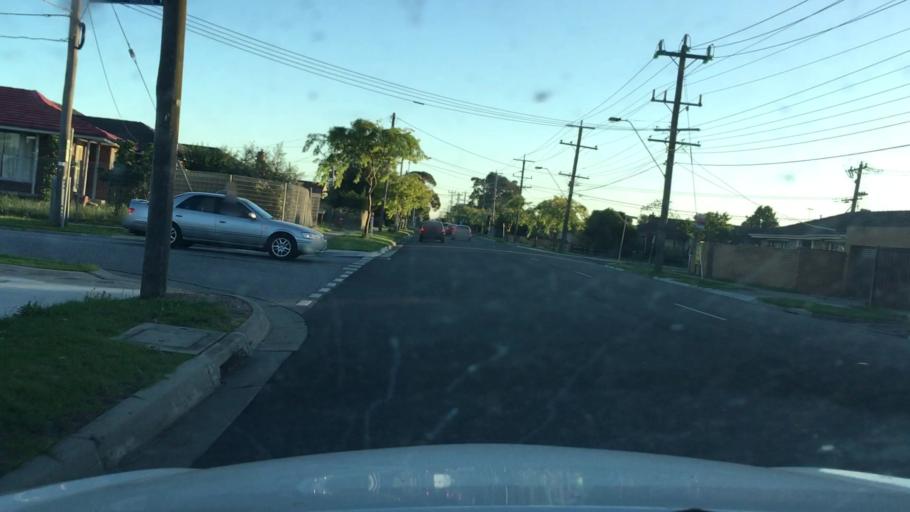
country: AU
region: Victoria
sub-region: Greater Dandenong
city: Noble Park
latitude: -37.9787
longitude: 145.1658
